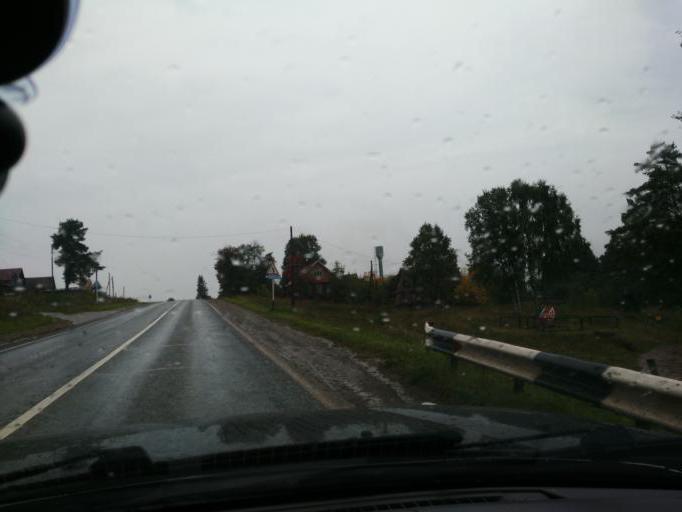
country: RU
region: Perm
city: Yugo-Kamskiy
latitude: 57.5545
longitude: 55.6855
